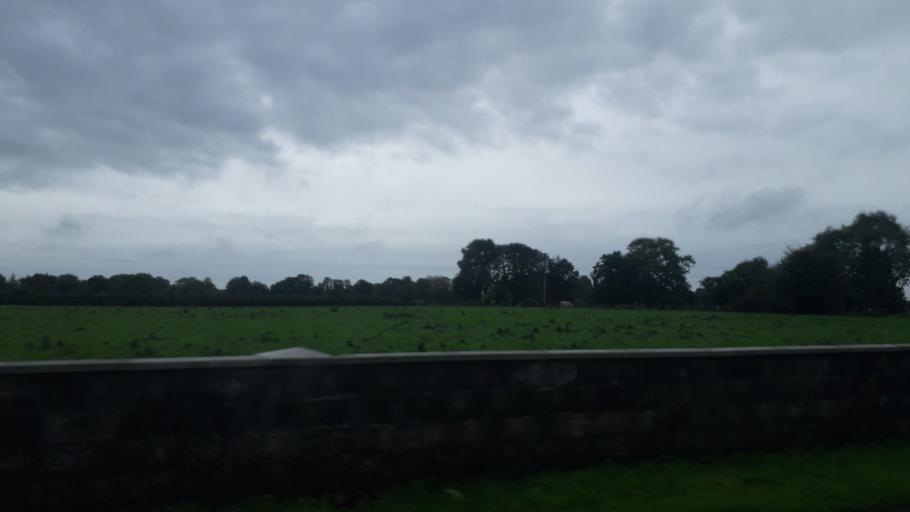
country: IE
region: Leinster
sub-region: An Longfort
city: Longford
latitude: 53.7288
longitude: -7.8946
